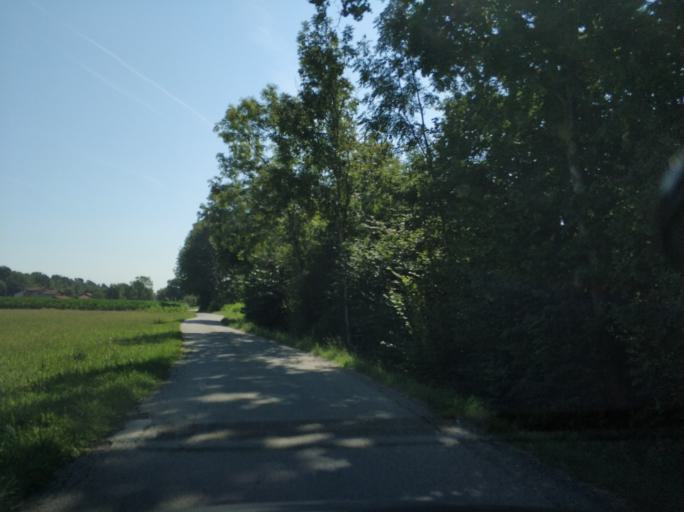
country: IT
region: Piedmont
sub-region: Provincia di Torino
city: San Maurizio
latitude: 45.2336
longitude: 7.6244
